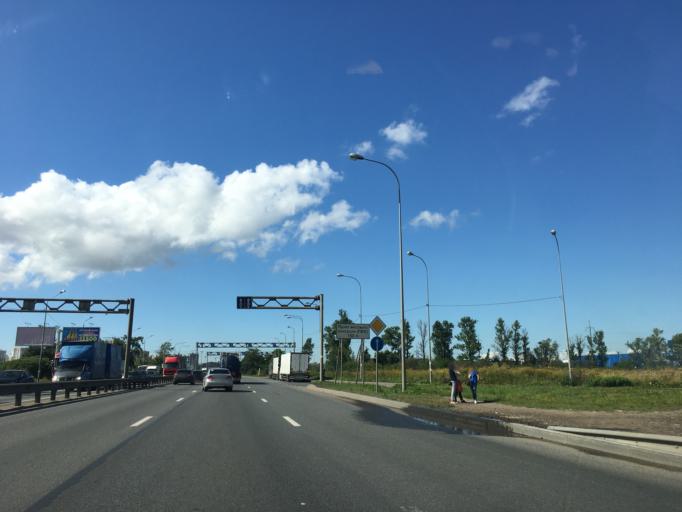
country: RU
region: St.-Petersburg
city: Shushary
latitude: 59.7988
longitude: 30.4041
